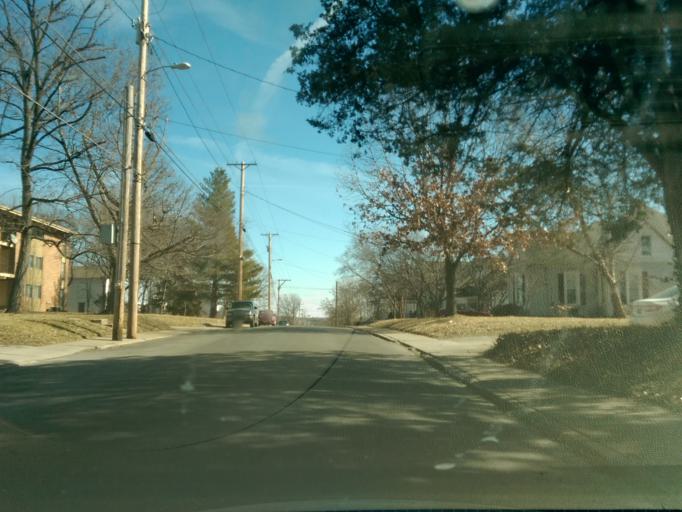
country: US
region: Missouri
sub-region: Boone County
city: Columbia
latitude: 38.9567
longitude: -92.3162
